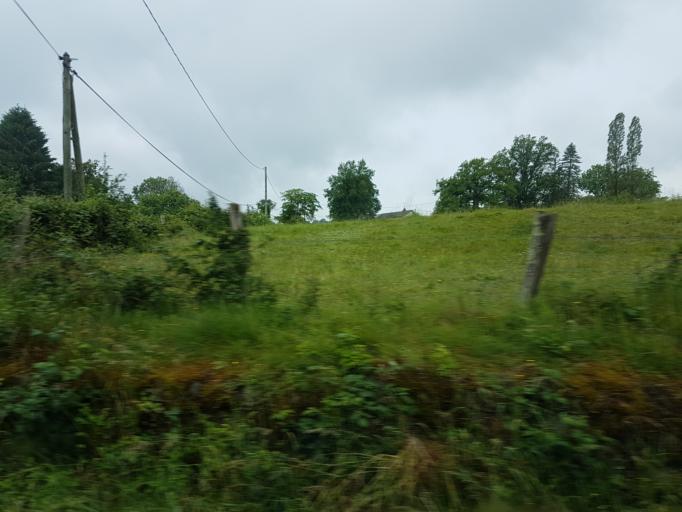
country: FR
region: Bourgogne
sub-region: Departement de la Nievre
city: Lormes
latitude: 47.1651
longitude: 3.8389
